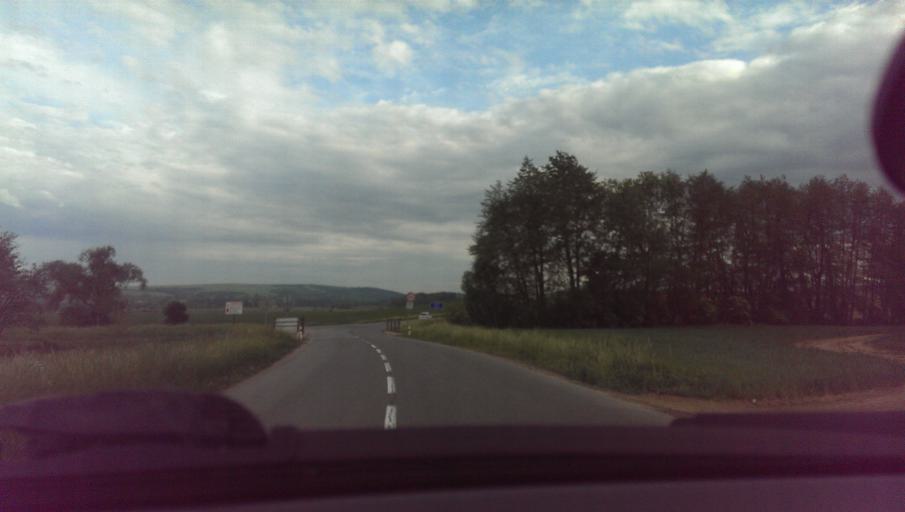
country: CZ
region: Zlin
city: Topolna
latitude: 49.1329
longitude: 17.5303
